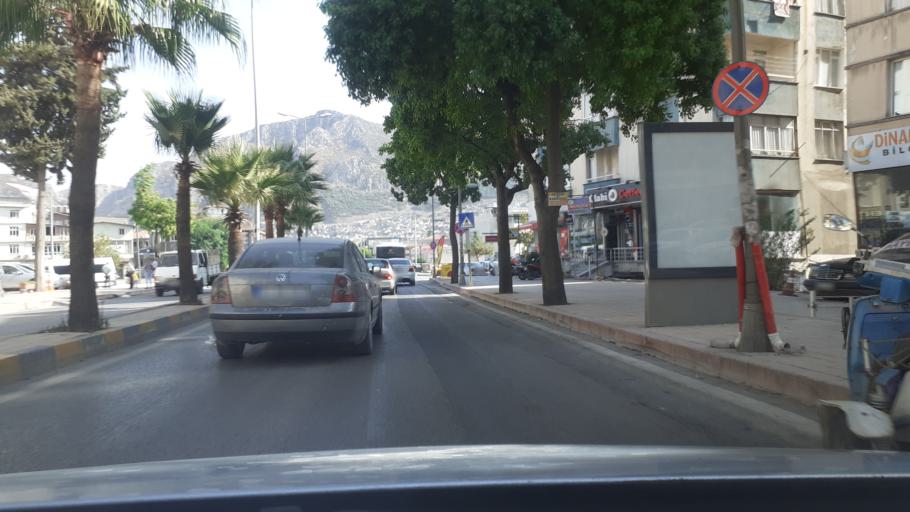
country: TR
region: Hatay
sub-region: Antakya Ilcesi
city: Antakya
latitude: 36.2103
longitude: 36.1608
